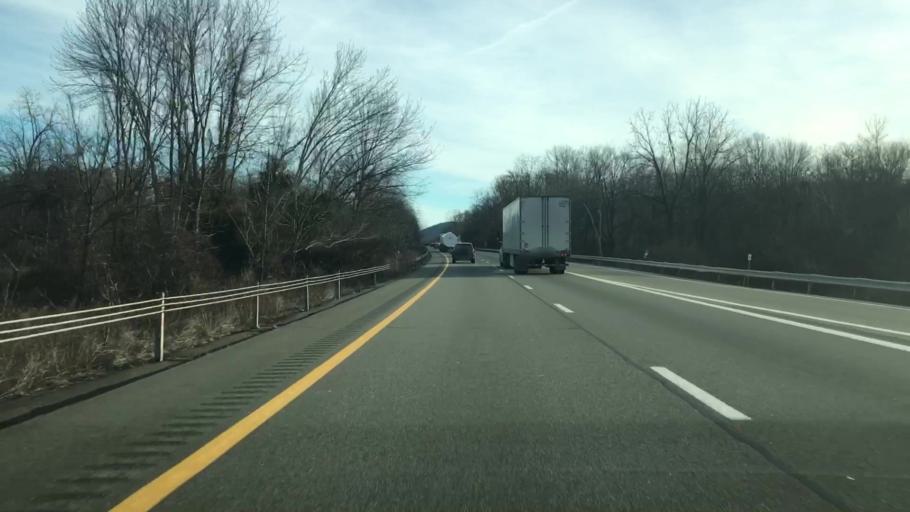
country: US
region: New York
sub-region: Dutchess County
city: Brinckerhoff
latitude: 41.5304
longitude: -73.8044
